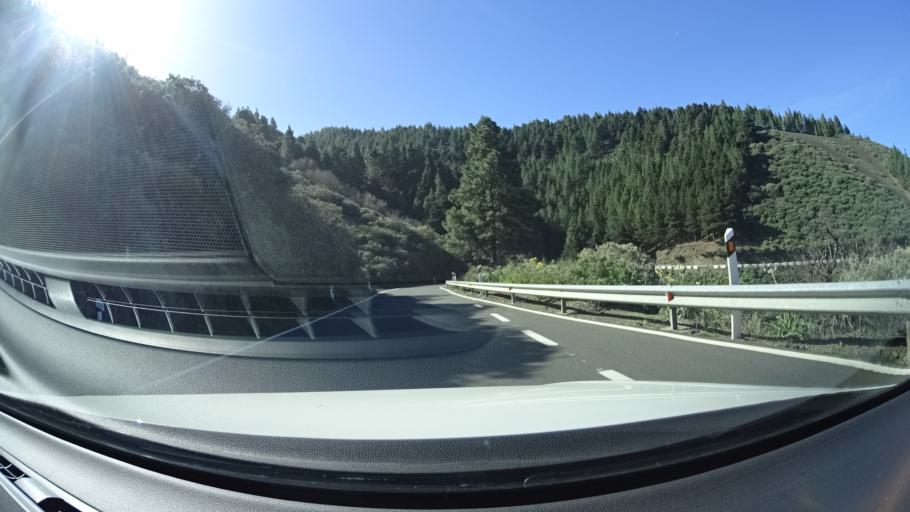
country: ES
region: Canary Islands
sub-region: Provincia de Las Palmas
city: Artenara
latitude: 28.0271
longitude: -15.6176
